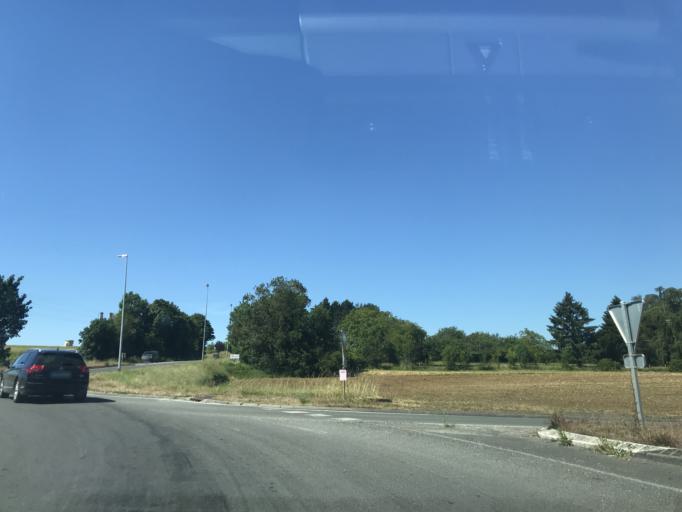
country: FR
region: Poitou-Charentes
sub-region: Departement de la Charente-Maritime
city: Pons
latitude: 45.5755
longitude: -0.5330
